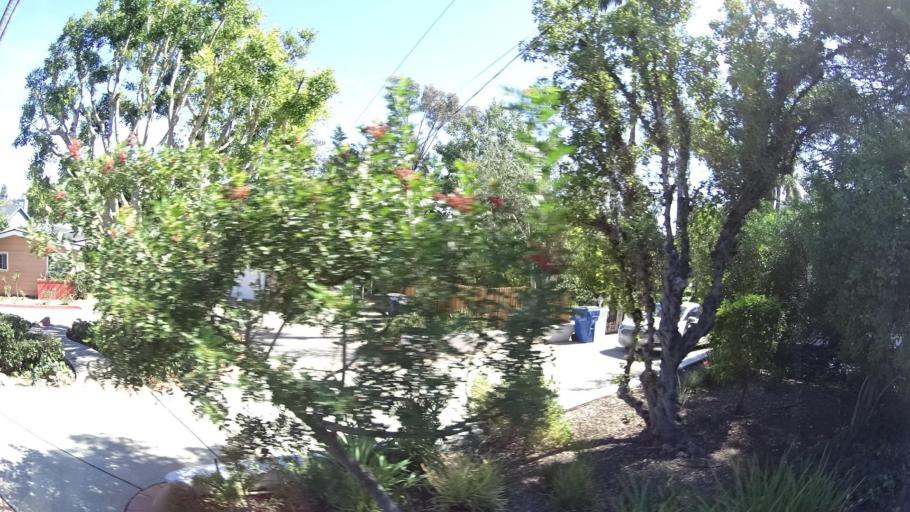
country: US
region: California
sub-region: San Diego County
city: Casa de Oro-Mount Helix
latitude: 32.7642
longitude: -116.9650
